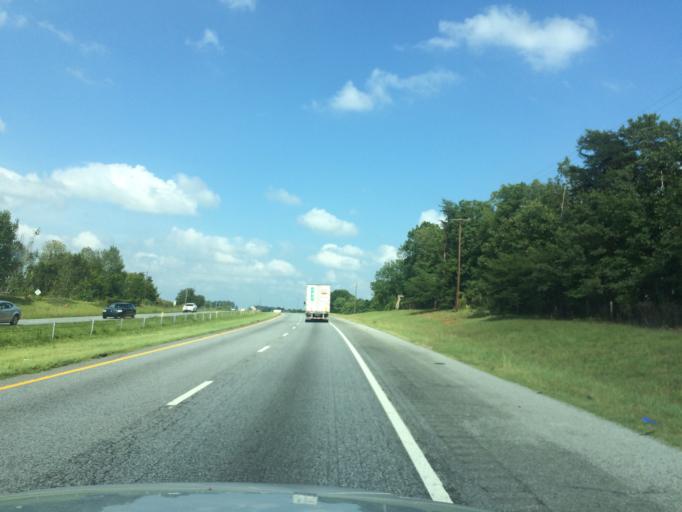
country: US
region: South Carolina
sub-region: Spartanburg County
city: Cowpens
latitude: 35.0559
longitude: -81.7875
